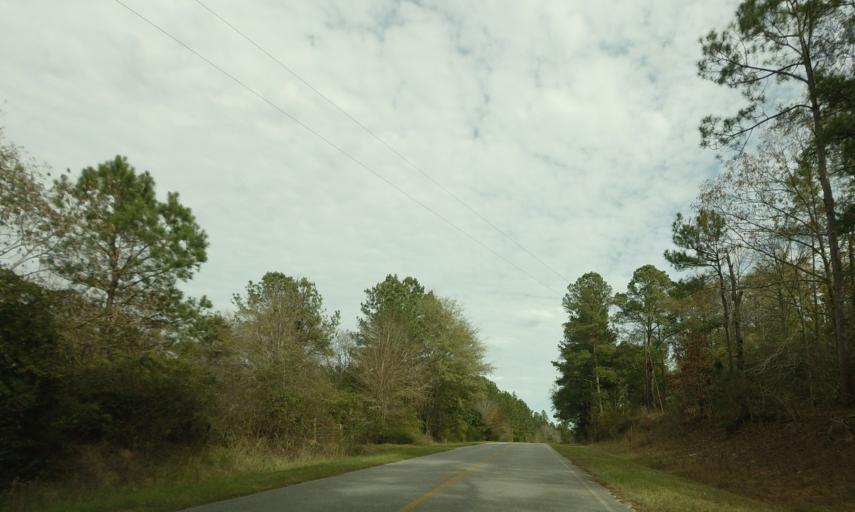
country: US
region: Georgia
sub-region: Dodge County
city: Chester
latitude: 32.4608
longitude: -83.1291
